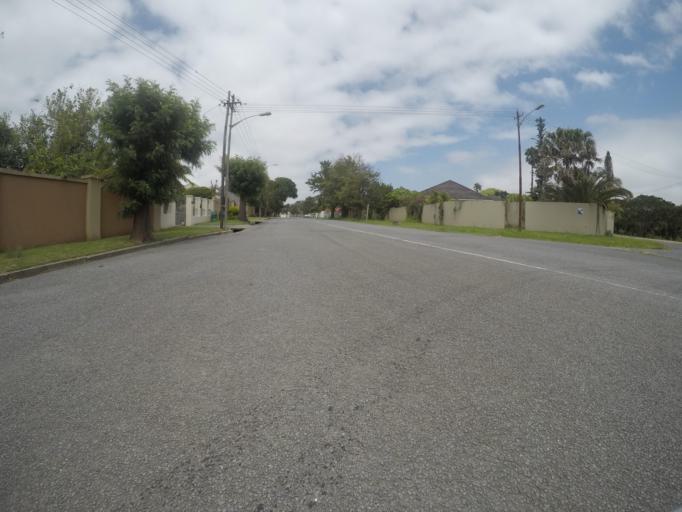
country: ZA
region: Eastern Cape
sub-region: Buffalo City Metropolitan Municipality
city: East London
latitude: -32.9893
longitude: 27.9263
